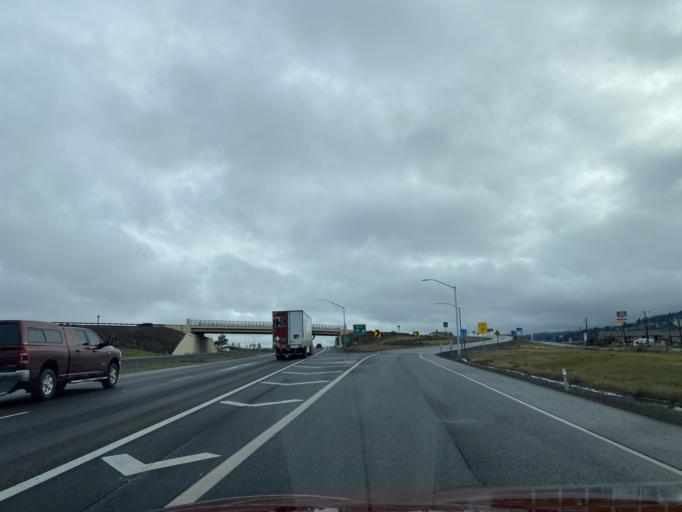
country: US
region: Oregon
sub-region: Jackson County
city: Talent
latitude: 42.2296
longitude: -122.7458
